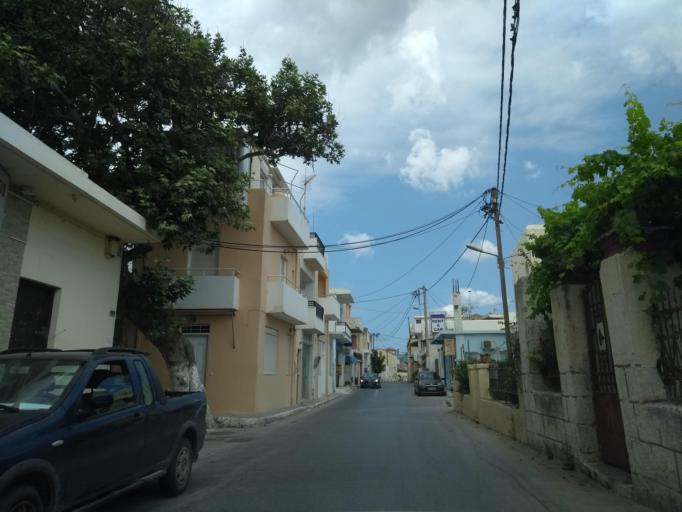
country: GR
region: Crete
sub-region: Nomos Chanias
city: Kalivai
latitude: 35.4541
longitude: 24.1713
